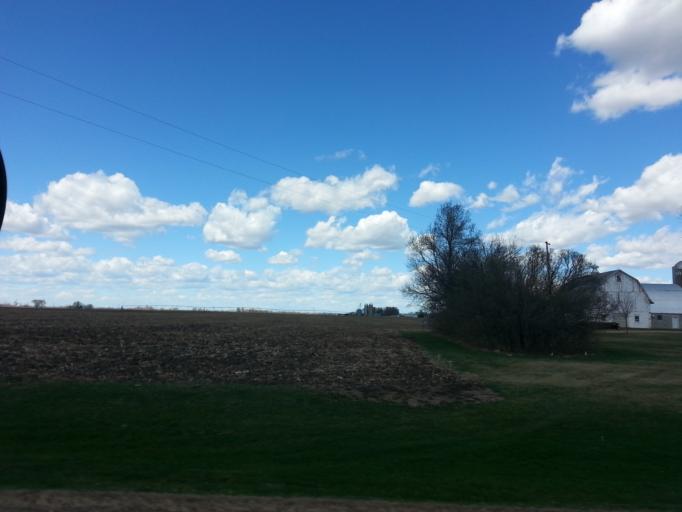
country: US
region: Minnesota
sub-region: Washington County
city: Cottage Grove
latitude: 44.7170
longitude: -92.9978
